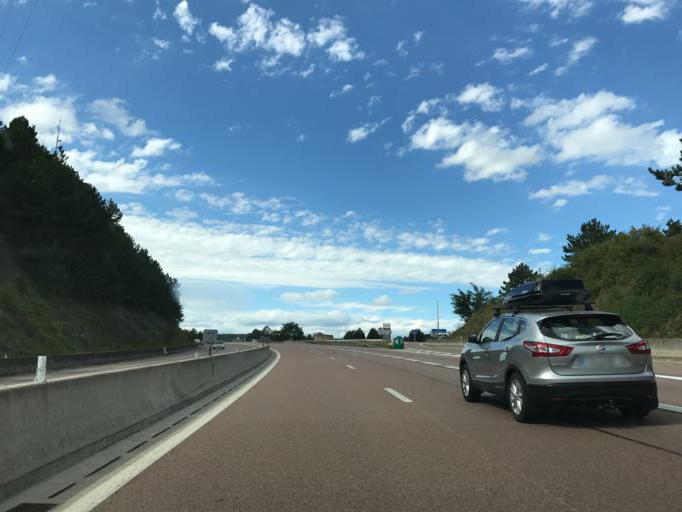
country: FR
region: Bourgogne
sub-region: Departement de la Cote-d'Or
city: Savigny-les-Beaune
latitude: 47.0543
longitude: 4.8296
